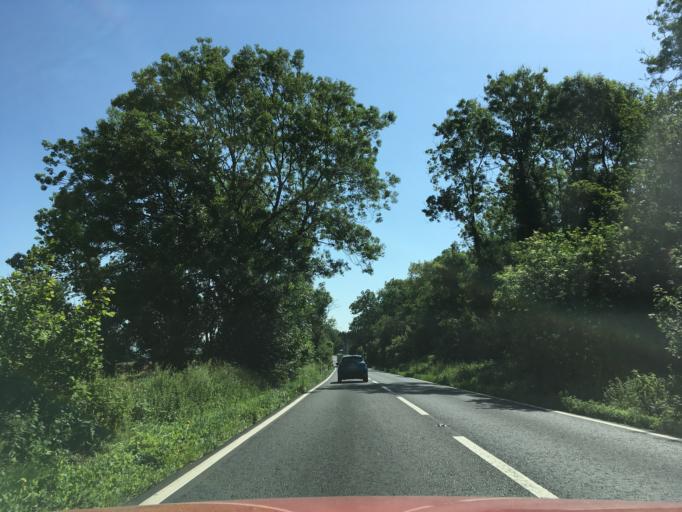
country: GB
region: England
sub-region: Gloucestershire
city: Charlton Kings
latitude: 51.8652
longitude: -2.0039
